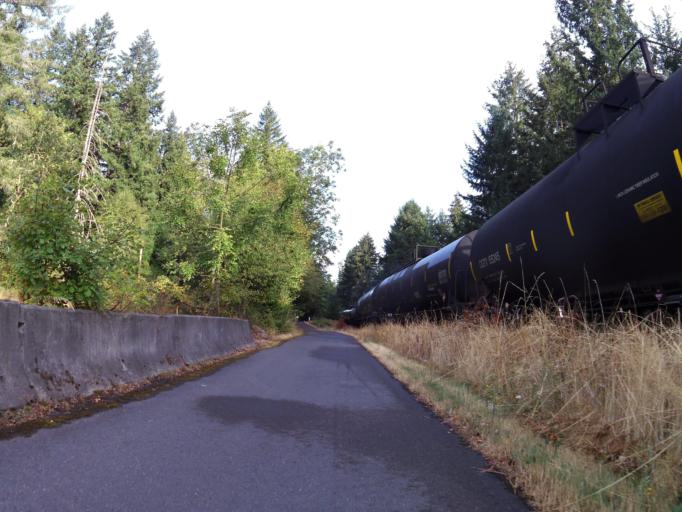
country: US
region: Washington
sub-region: Thurston County
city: Rainier
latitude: 46.9053
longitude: -122.7708
